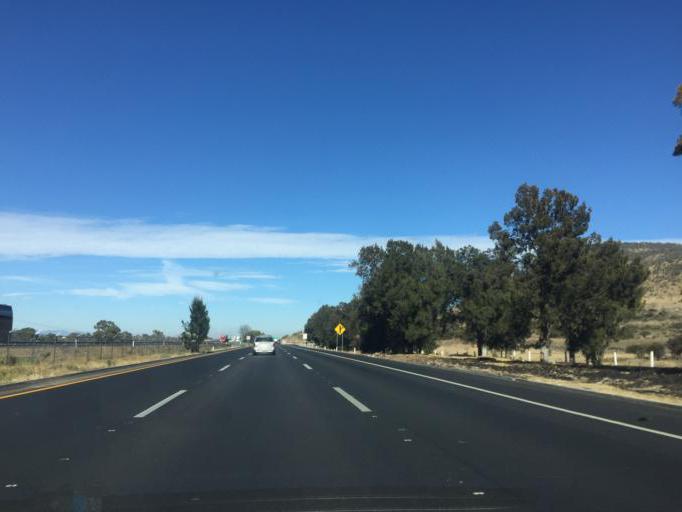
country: MX
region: Mexico
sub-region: Aculco
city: La Presita Segundo Cuartel
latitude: 20.2115
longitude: -99.7929
